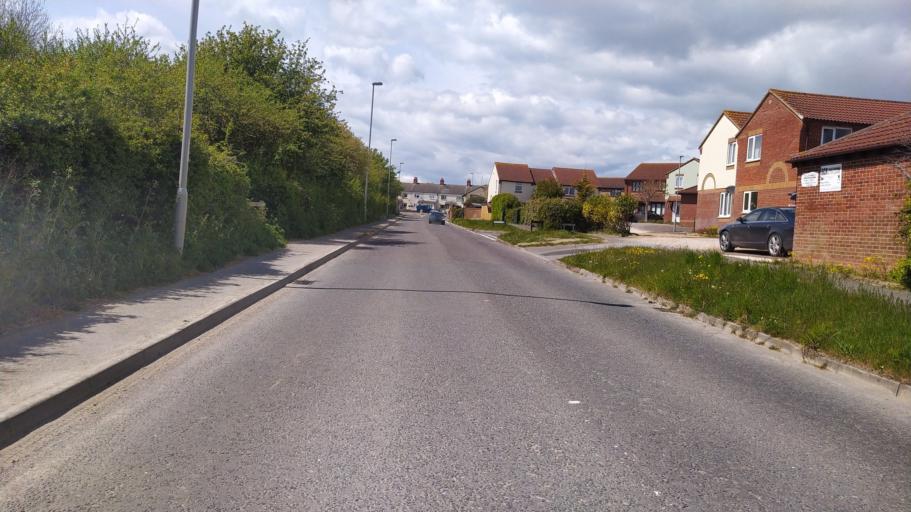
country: GB
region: England
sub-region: Dorset
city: Chickerell
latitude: 50.6181
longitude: -2.4989
